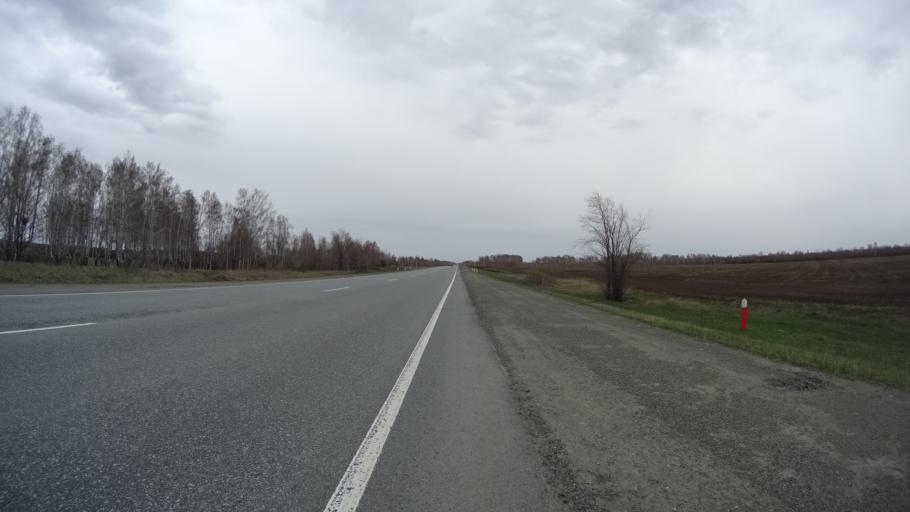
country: RU
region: Chelyabinsk
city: Krasnogorskiy
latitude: 54.6592
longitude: 61.2556
